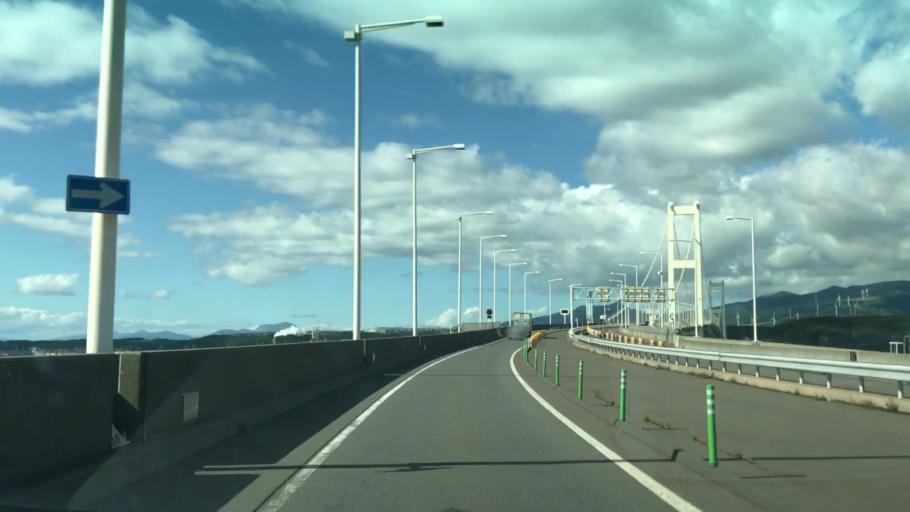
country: JP
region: Hokkaido
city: Muroran
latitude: 42.3438
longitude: 140.9492
